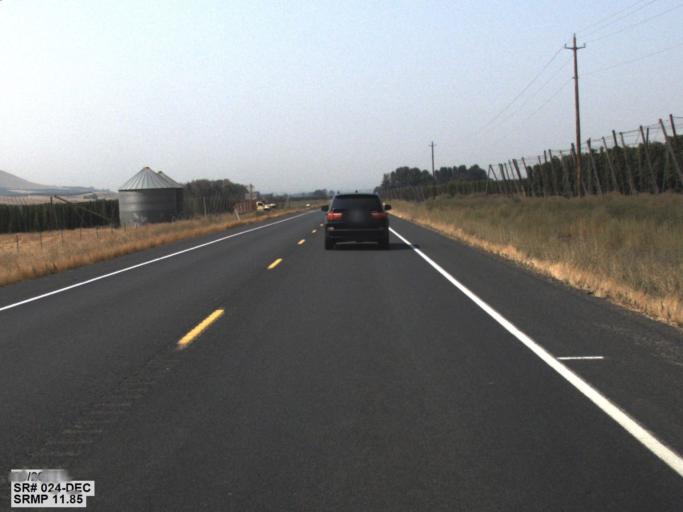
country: US
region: Washington
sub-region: Yakima County
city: Zillah
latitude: 46.5251
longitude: -120.2514
